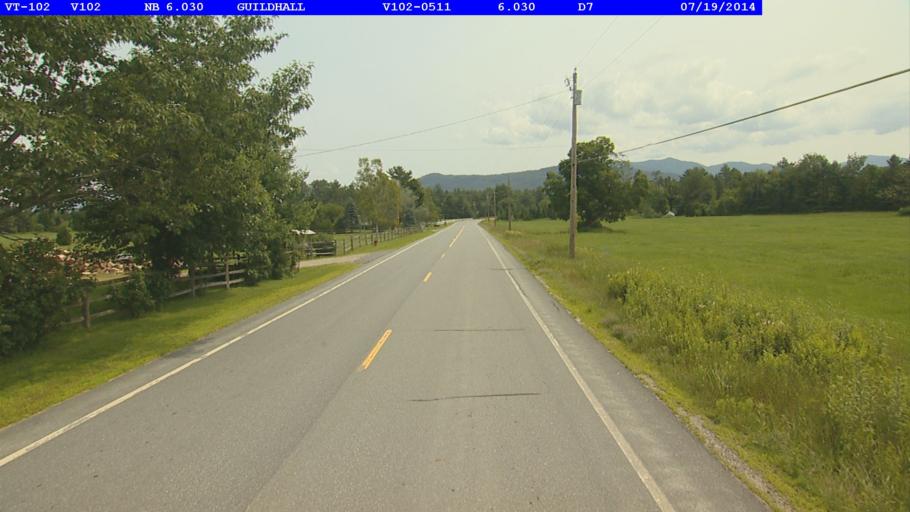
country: US
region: Vermont
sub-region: Essex County
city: Guildhall
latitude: 44.5666
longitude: -71.5850
